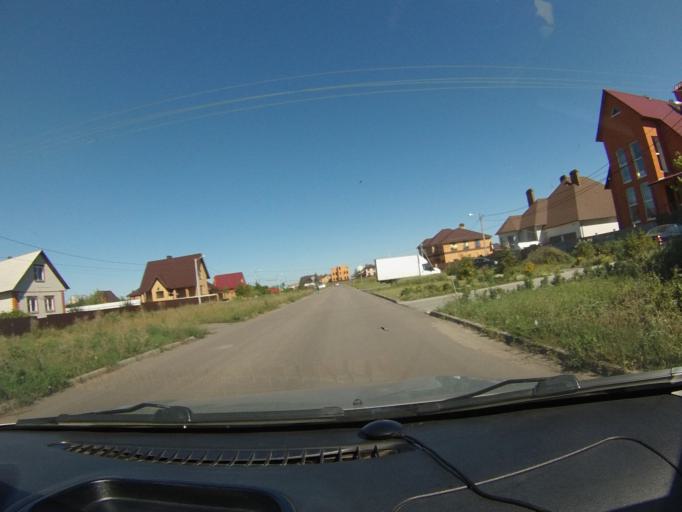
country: RU
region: Tambov
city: Tambov
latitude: 52.7805
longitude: 41.3852
